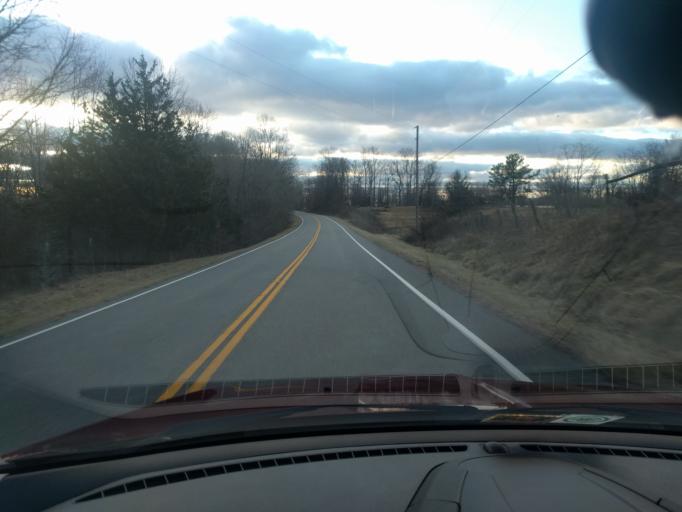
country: US
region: Virginia
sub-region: City of Bedford
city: Bedford
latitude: 37.4115
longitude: -79.5649
